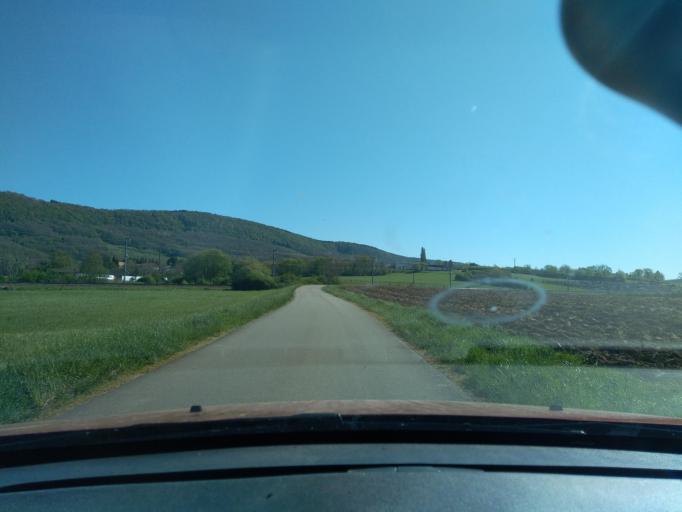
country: FR
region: Franche-Comte
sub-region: Departement du Jura
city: Cousance
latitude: 46.5837
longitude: 5.4404
